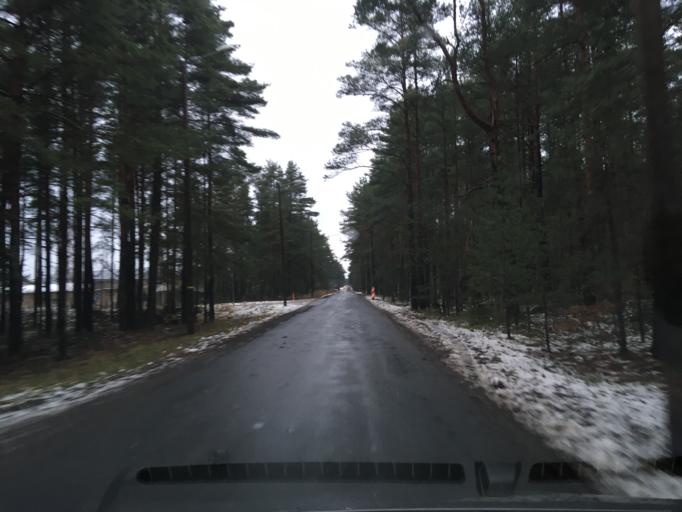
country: EE
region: Harju
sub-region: Tallinna linn
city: Tallinn
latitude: 59.3821
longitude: 24.7285
